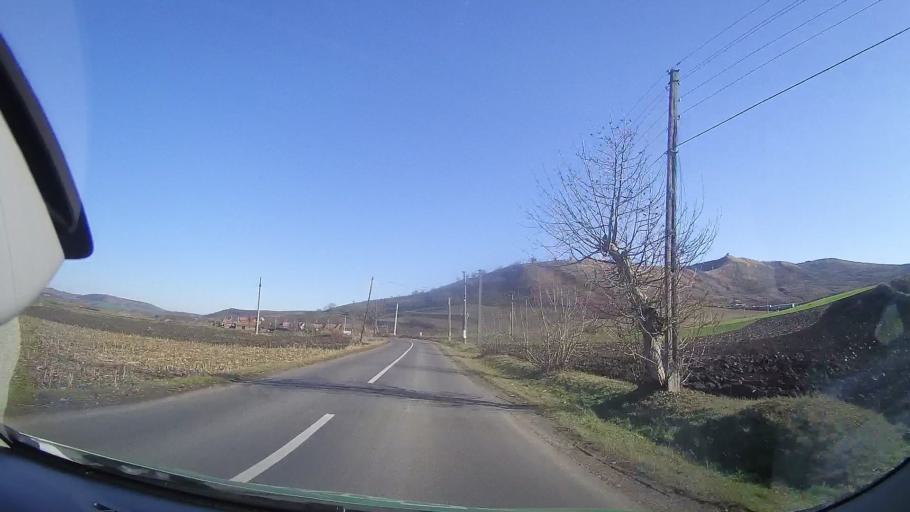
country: RO
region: Mures
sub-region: Comuna Band
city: Band
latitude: 46.5624
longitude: 24.3365
